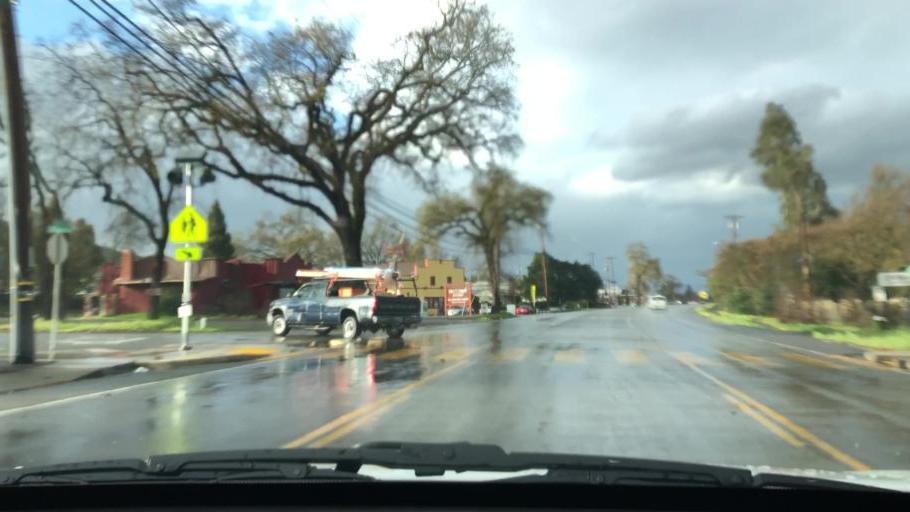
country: US
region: California
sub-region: Mendocino County
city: Ukiah
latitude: 39.1239
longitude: -123.2044
